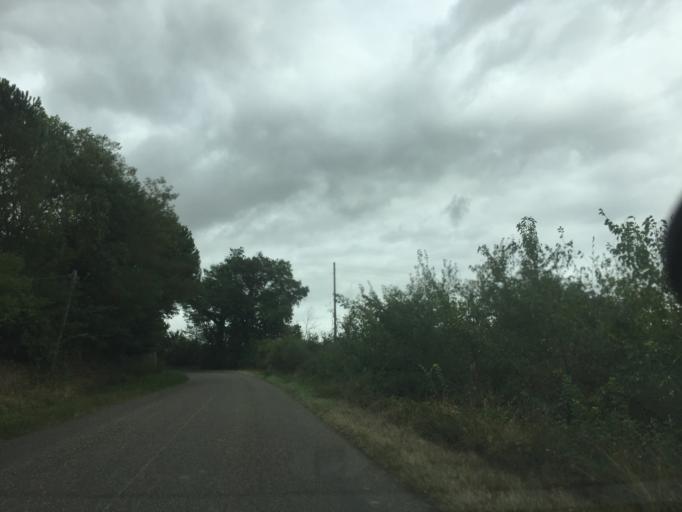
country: FR
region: Midi-Pyrenees
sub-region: Departement du Gers
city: Mirande
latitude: 43.5945
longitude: 0.3228
